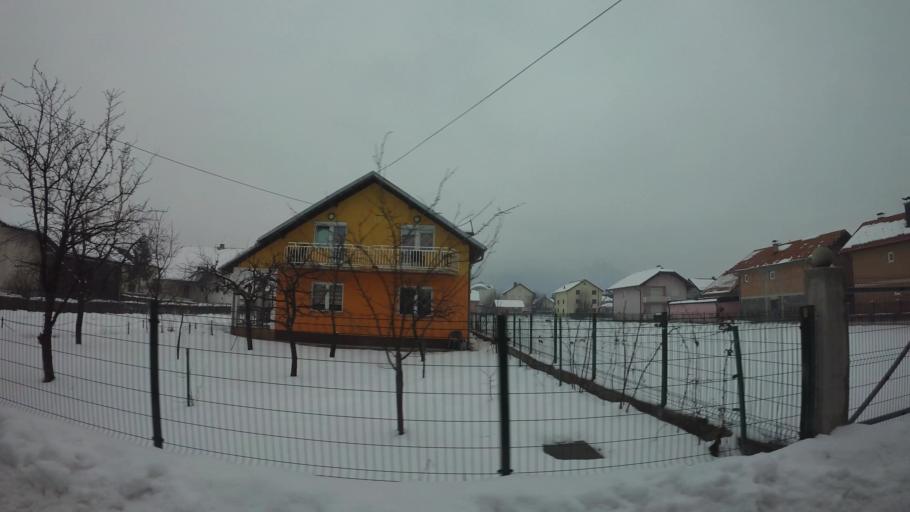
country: BA
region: Federation of Bosnia and Herzegovina
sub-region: Kanton Sarajevo
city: Sarajevo
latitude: 43.8445
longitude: 18.2805
